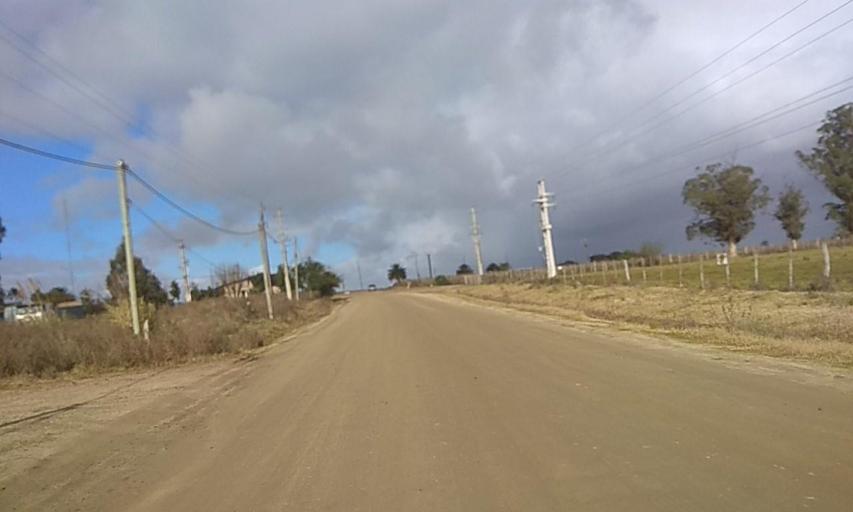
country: UY
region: Florida
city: Florida
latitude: -34.0946
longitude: -56.1898
